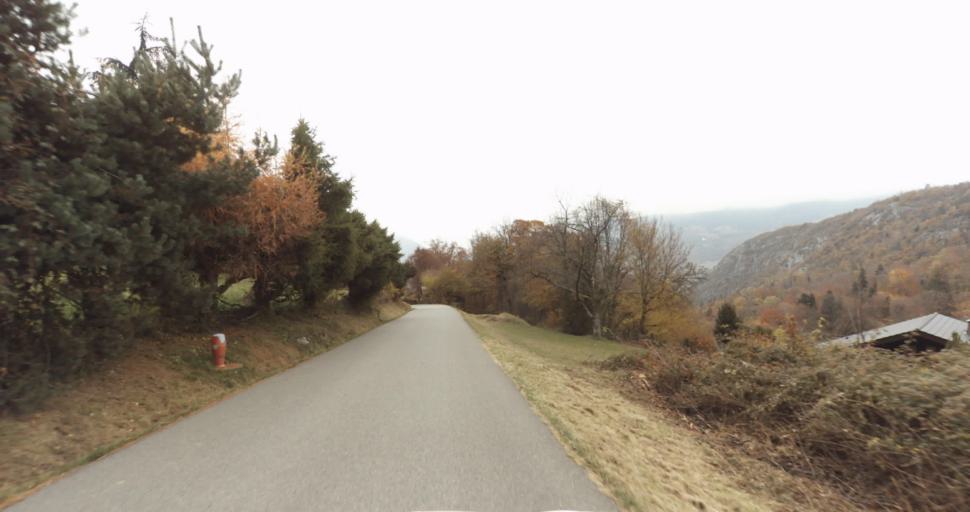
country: FR
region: Rhone-Alpes
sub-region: Departement de la Haute-Savoie
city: Talloires
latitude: 45.8178
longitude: 6.1952
